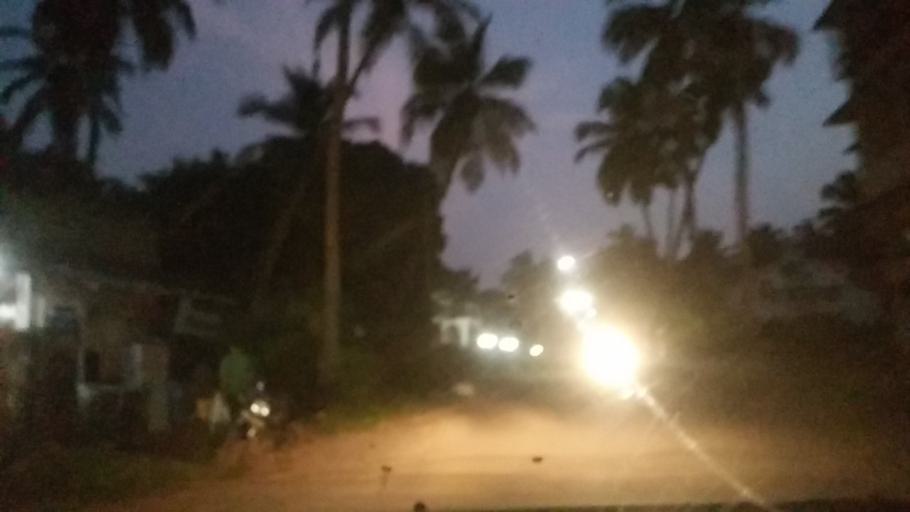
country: IN
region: Goa
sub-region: South Goa
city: Madgaon
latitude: 15.2636
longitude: 73.9648
